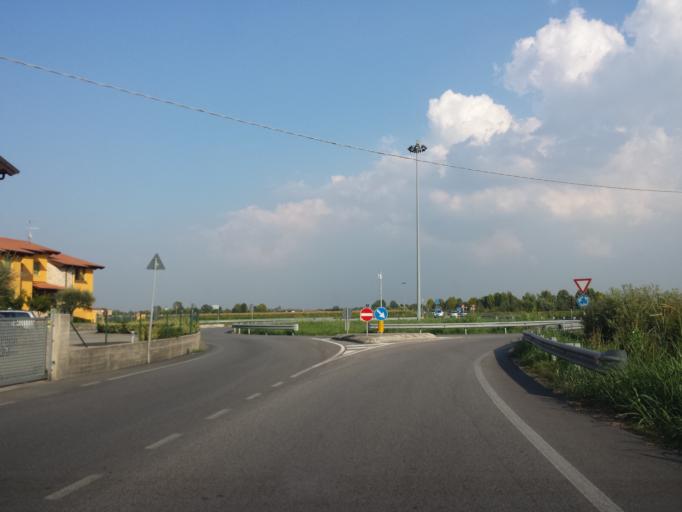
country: IT
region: Veneto
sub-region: Provincia di Vicenza
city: Torri di Quartesolo
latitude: 45.5153
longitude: 11.6331
